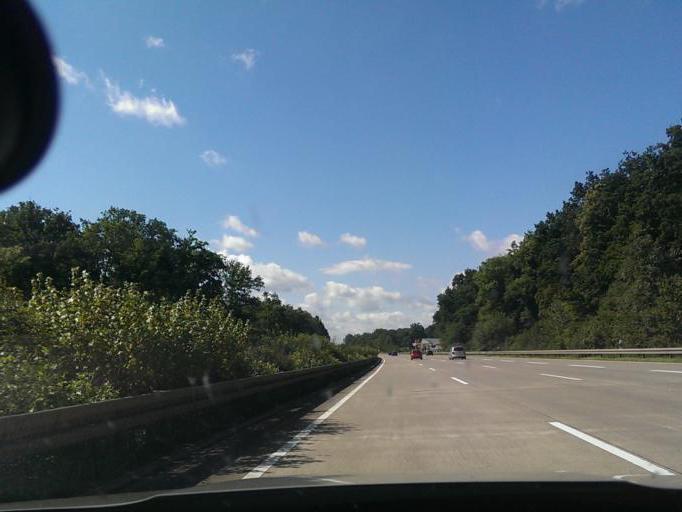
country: DE
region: Lower Saxony
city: Laatzen
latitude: 52.3438
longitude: 9.8684
